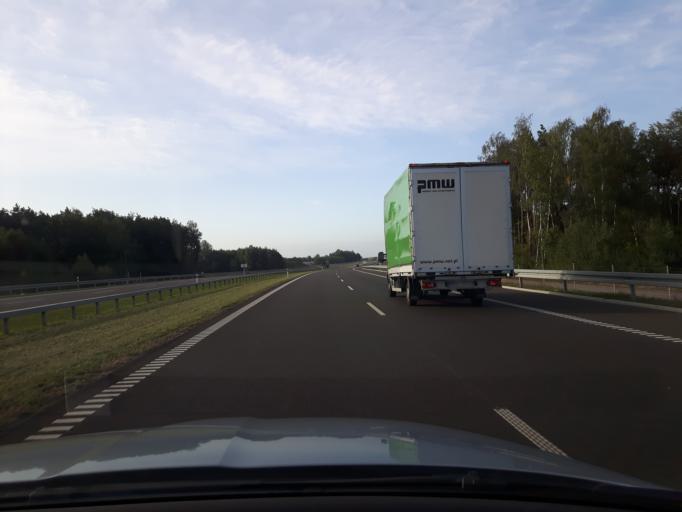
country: PL
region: Masovian Voivodeship
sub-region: Powiat radomski
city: Jedlinsk
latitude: 51.5208
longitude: 21.0851
